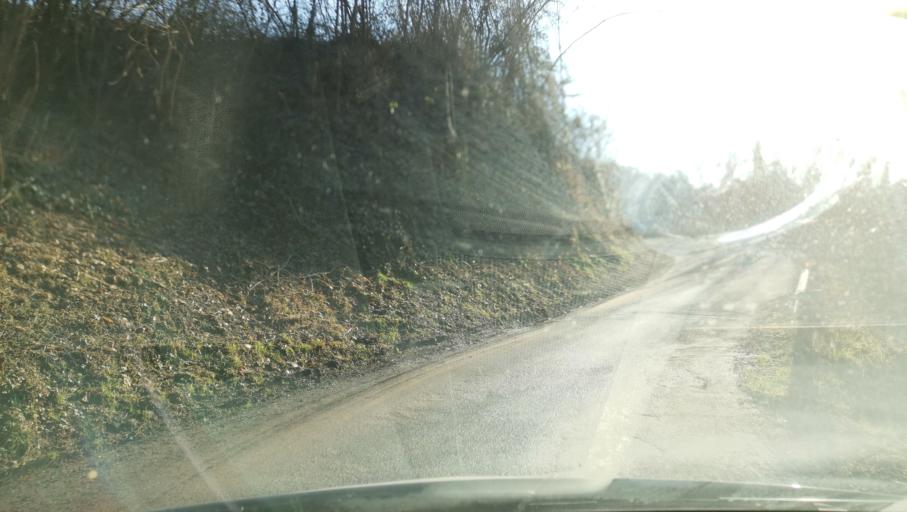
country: IT
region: Piedmont
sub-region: Provincia di Torino
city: San Raffaele Cimena
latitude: 45.1387
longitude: 7.8613
